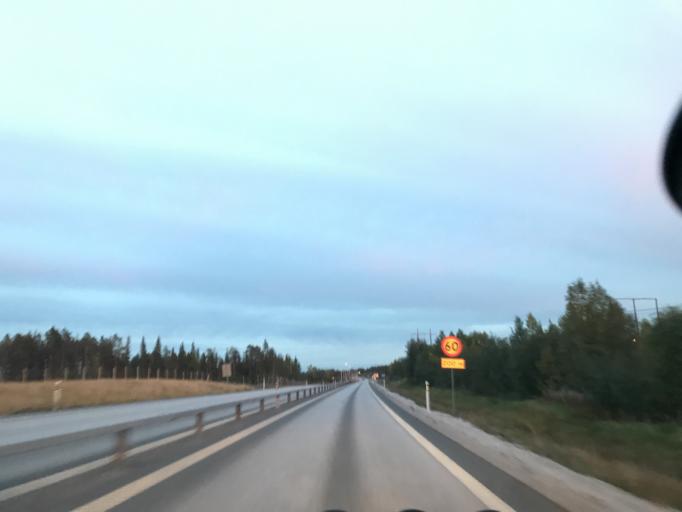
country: SE
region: Norrbotten
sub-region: Gallivare Kommun
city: Malmberget
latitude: 67.6570
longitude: 21.0093
